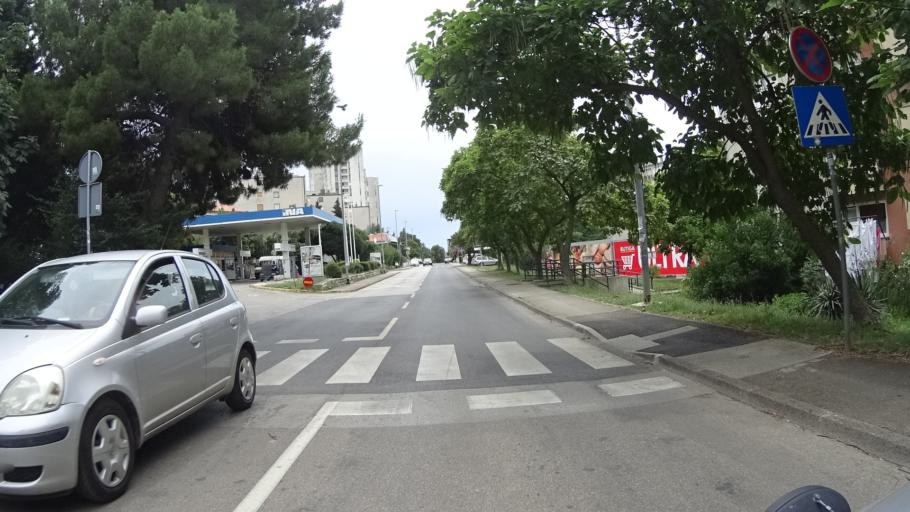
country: HR
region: Istarska
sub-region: Grad Pula
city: Pula
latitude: 44.8559
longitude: 13.8431
